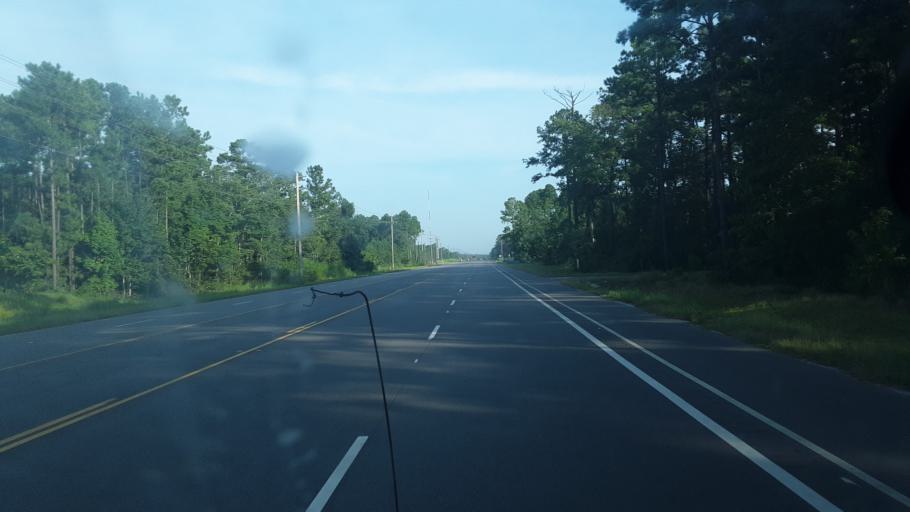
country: US
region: South Carolina
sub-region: Horry County
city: Myrtle Beach
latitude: 33.7701
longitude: -78.8679
